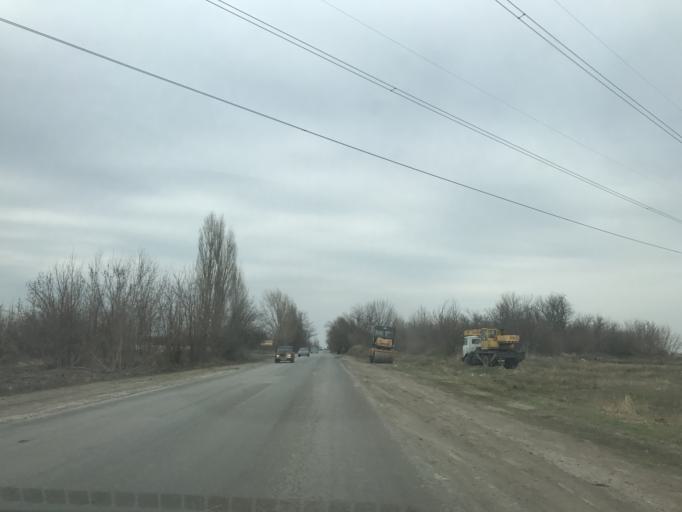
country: RU
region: Rostov
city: Novocherkassk
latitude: 47.3882
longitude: 40.0528
